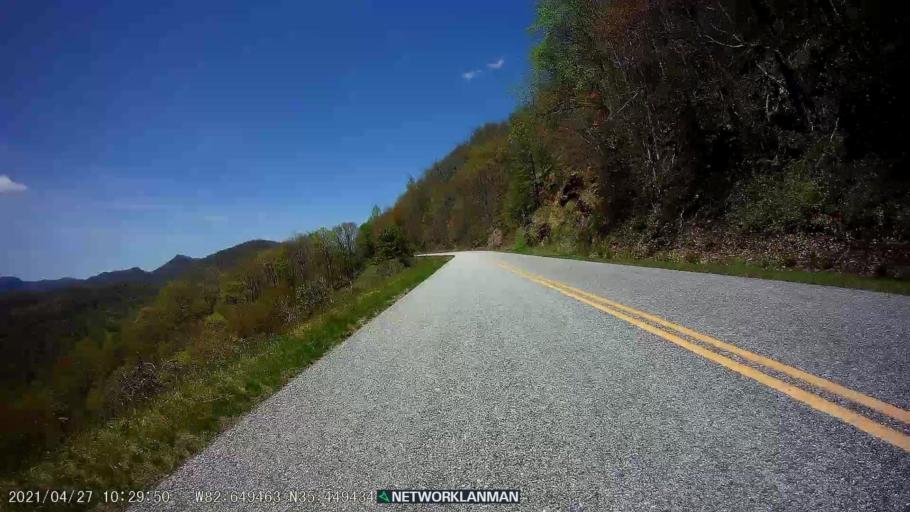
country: US
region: North Carolina
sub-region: Buncombe County
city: Avery Creek
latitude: 35.4490
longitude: -82.6508
